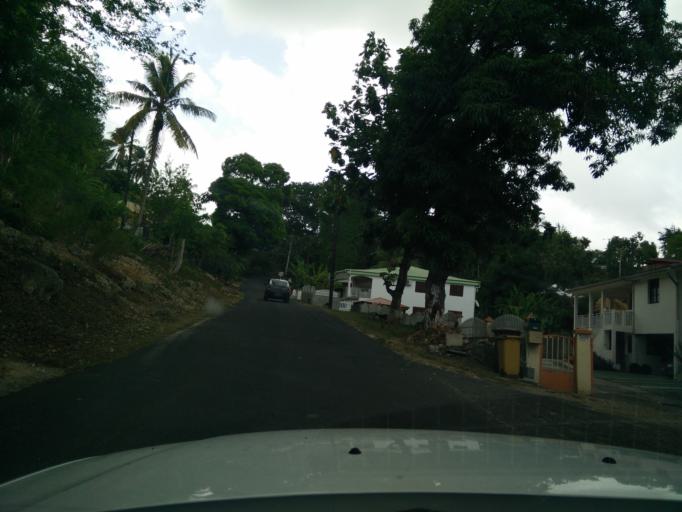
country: GP
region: Guadeloupe
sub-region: Guadeloupe
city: Le Gosier
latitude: 16.2287
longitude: -61.4596
